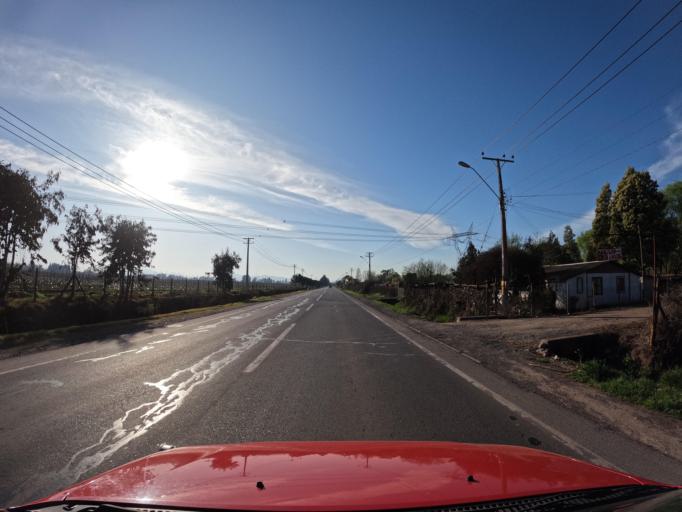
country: CL
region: Maule
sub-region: Provincia de Curico
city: Teno
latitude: -34.8813
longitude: -71.0786
